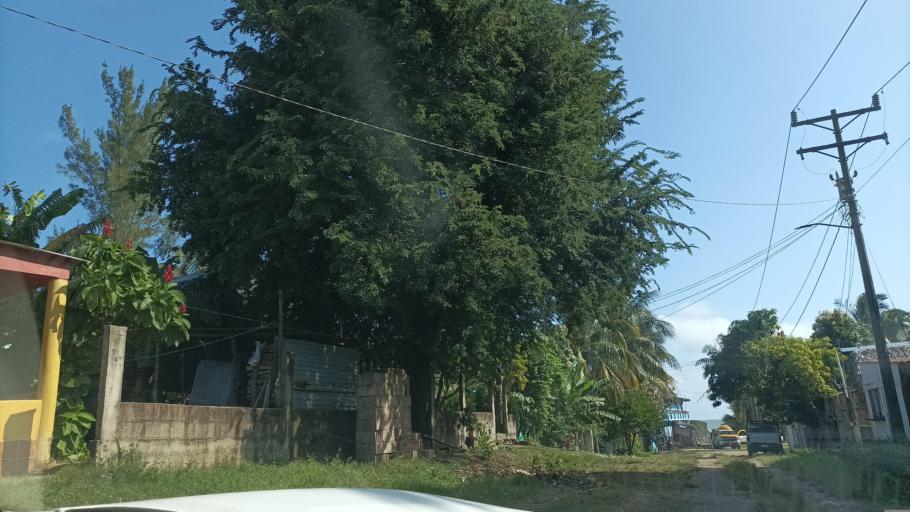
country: MX
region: Veracruz
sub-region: Coatzacoalcos
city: Fraccionamiento Ciudad Olmeca
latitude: 18.2126
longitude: -94.6118
